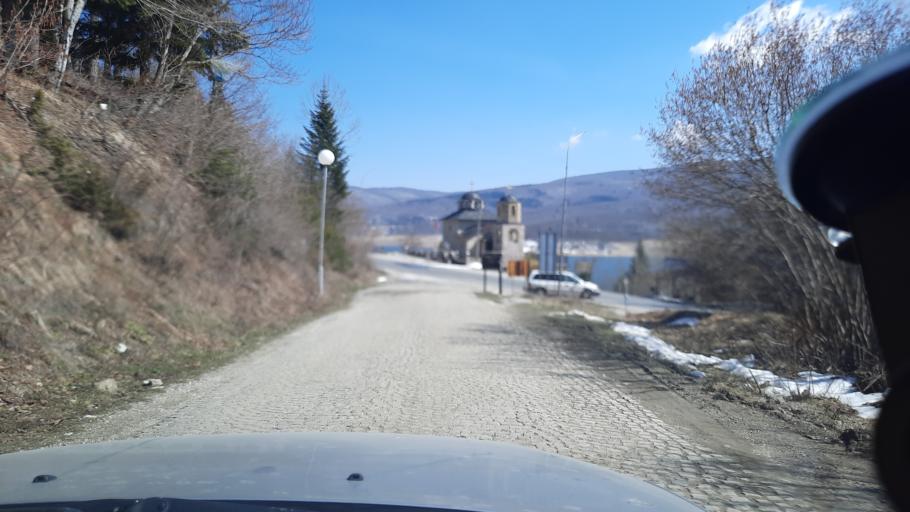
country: MK
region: Gostivar
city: Vrutok
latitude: 41.7035
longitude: 20.7587
